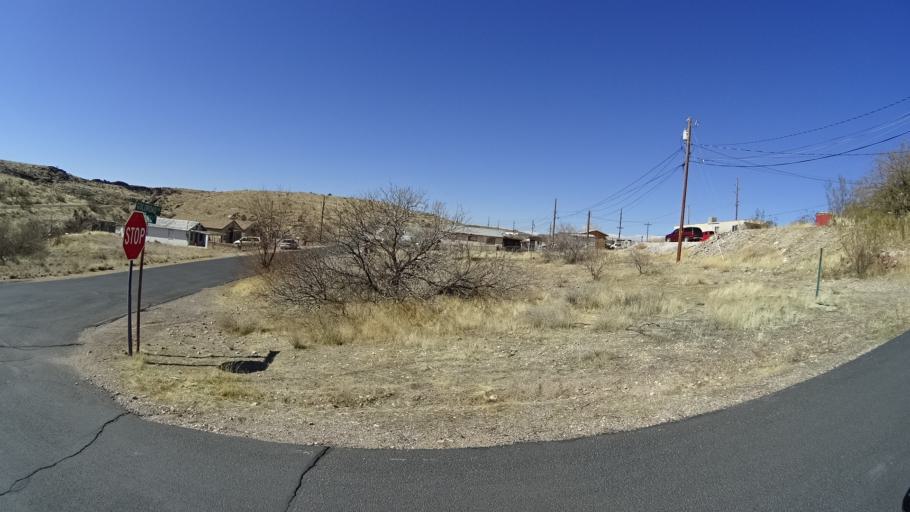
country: US
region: Arizona
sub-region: Mohave County
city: Kingman
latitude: 35.1846
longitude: -114.0551
